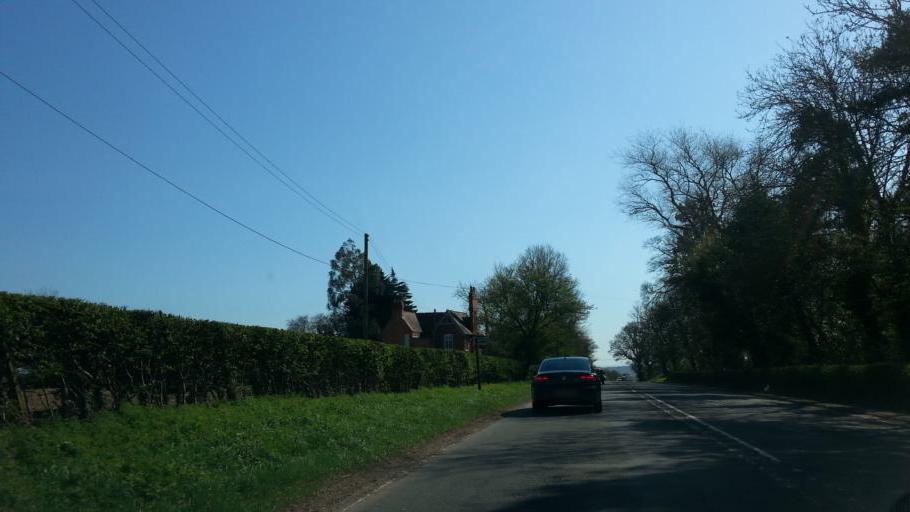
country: GB
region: England
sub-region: Worcestershire
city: Alvechurch
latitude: 52.3831
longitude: -1.9574
